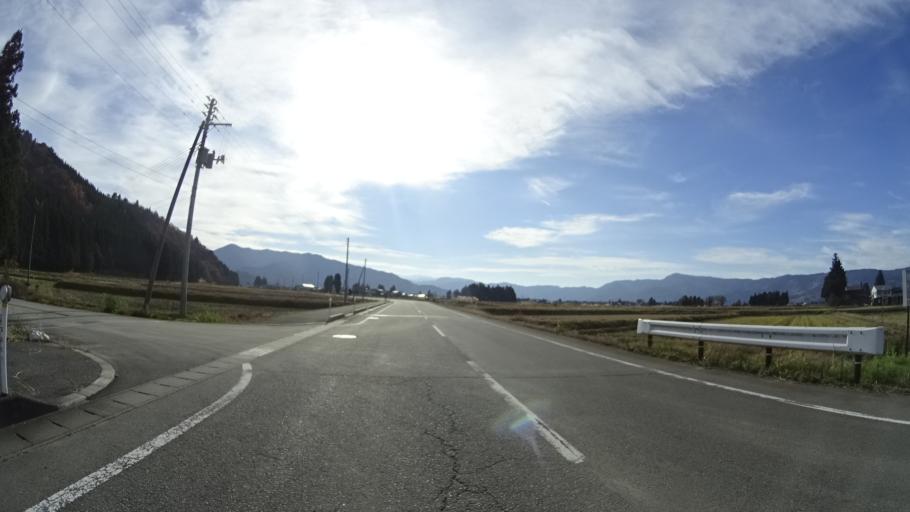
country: JP
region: Niigata
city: Muikamachi
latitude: 37.0308
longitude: 138.8844
